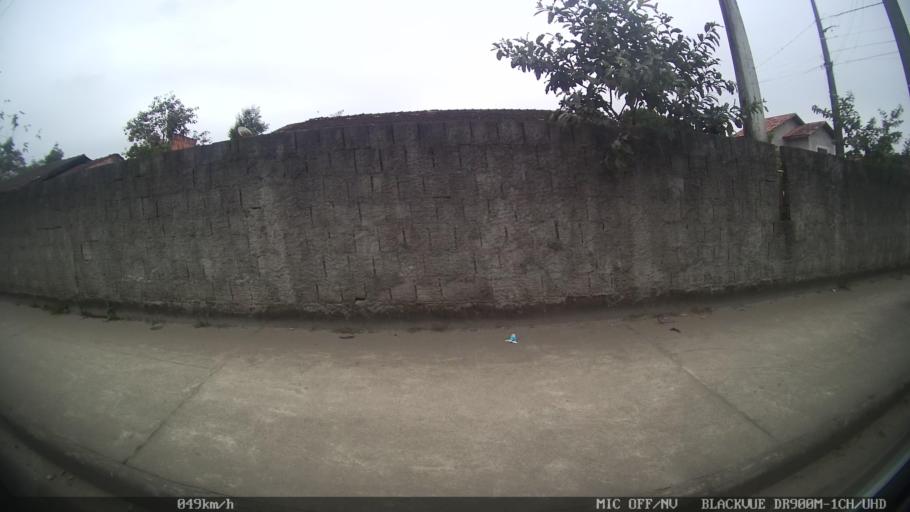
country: BR
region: Santa Catarina
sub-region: Joinville
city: Joinville
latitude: -26.2546
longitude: -48.8027
